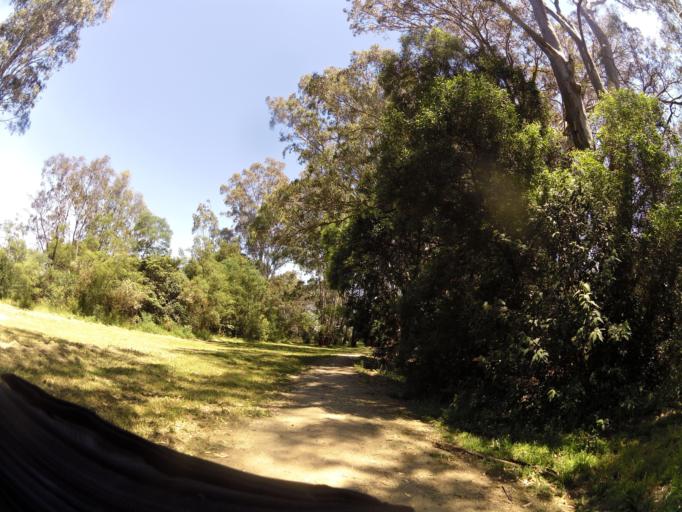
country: AU
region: Victoria
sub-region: Wellington
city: Sale
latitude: -37.9690
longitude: 146.9743
